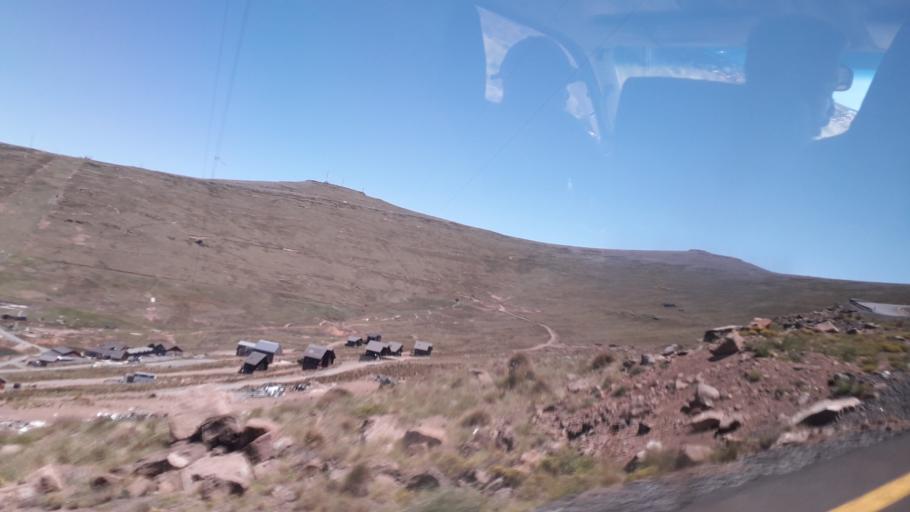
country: ZA
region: Orange Free State
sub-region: Thabo Mofutsanyana District Municipality
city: Phuthaditjhaba
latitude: -28.8257
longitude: 28.7312
